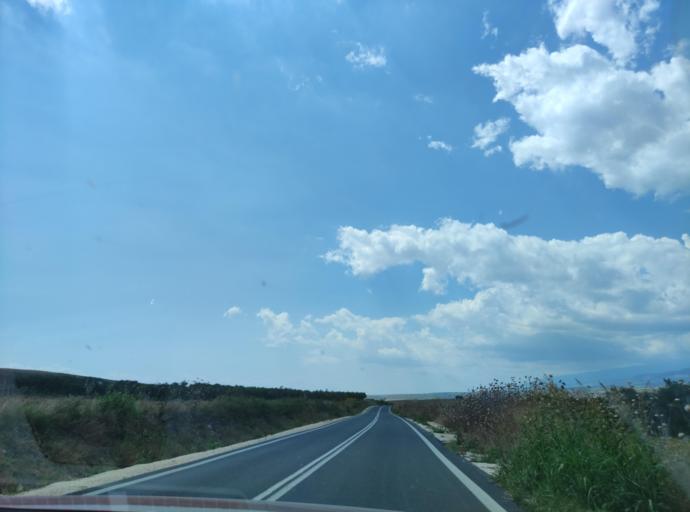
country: GR
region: Central Macedonia
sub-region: Nomos Serron
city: Proti
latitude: 40.9968
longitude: 23.9590
